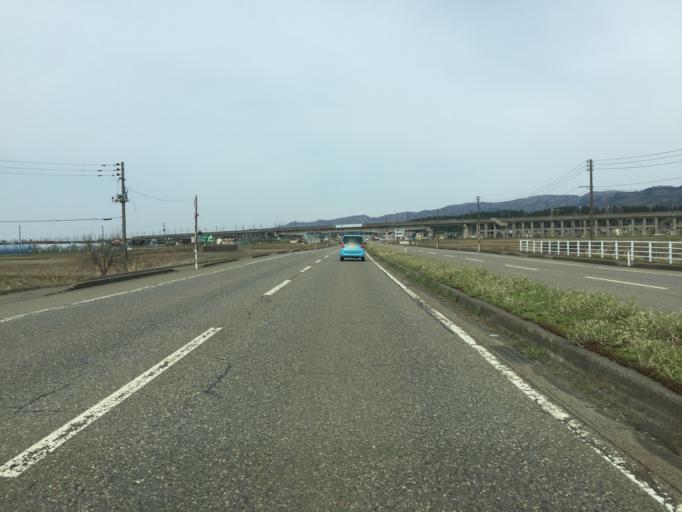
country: JP
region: Niigata
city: Nagaoka
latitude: 37.3988
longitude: 138.8413
